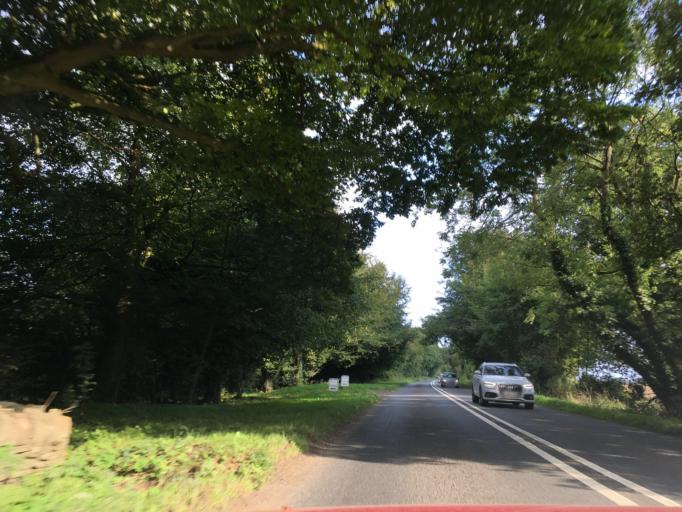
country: GB
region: England
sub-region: Gloucestershire
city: Nailsworth
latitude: 51.6617
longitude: -2.2686
